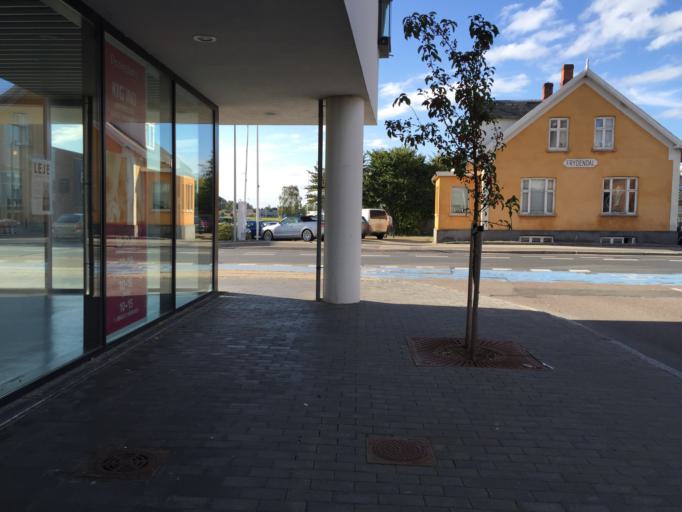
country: DK
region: Capital Region
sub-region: Hillerod Kommune
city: Hillerod
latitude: 55.9290
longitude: 12.2944
